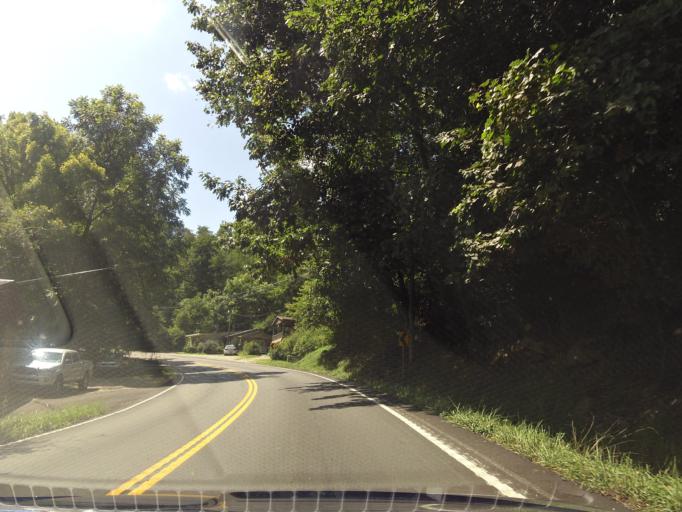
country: US
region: Kentucky
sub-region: Harlan County
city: Loyall
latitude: 36.9034
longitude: -83.3428
